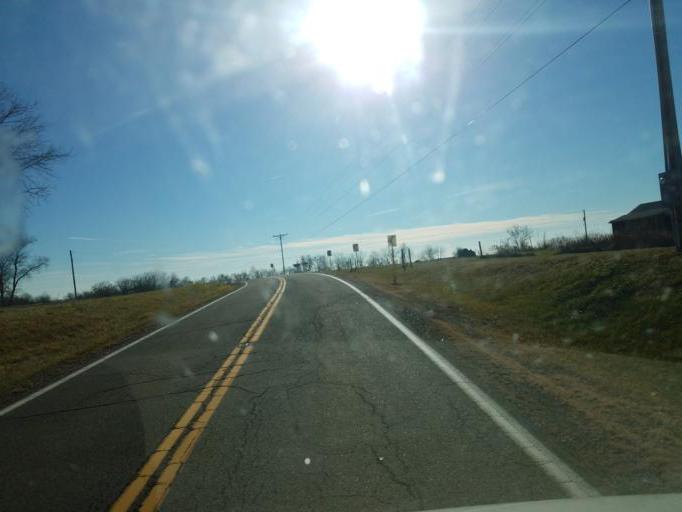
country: US
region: Ohio
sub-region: Knox County
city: Oak Hill
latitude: 40.2831
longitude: -82.1417
